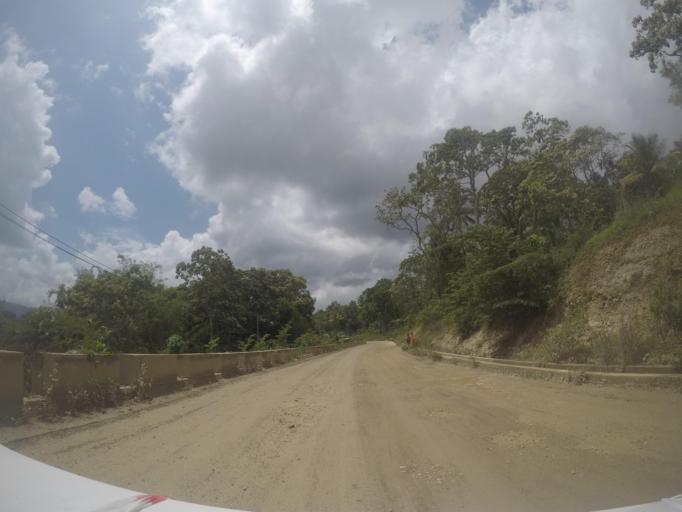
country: TL
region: Baucau
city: Venilale
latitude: -8.5877
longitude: 126.3874
